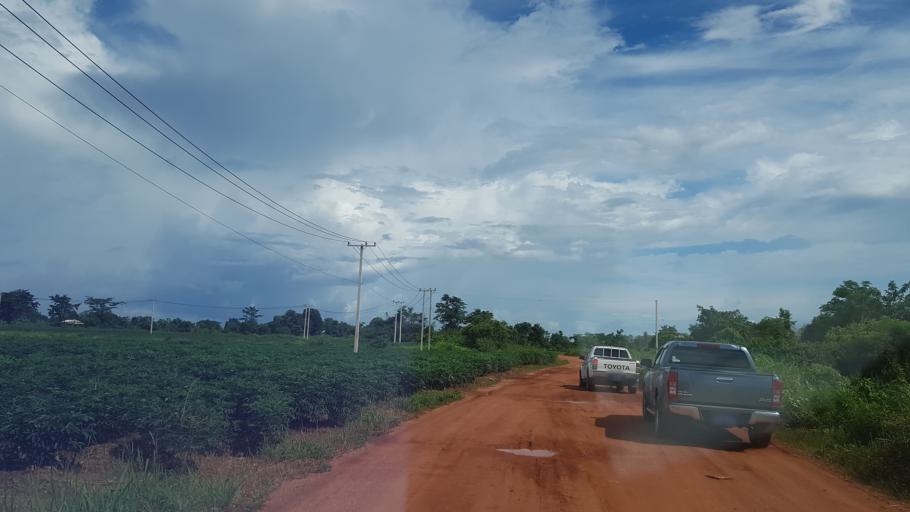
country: LA
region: Vientiane
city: Vientiane
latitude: 18.2067
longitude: 102.5678
